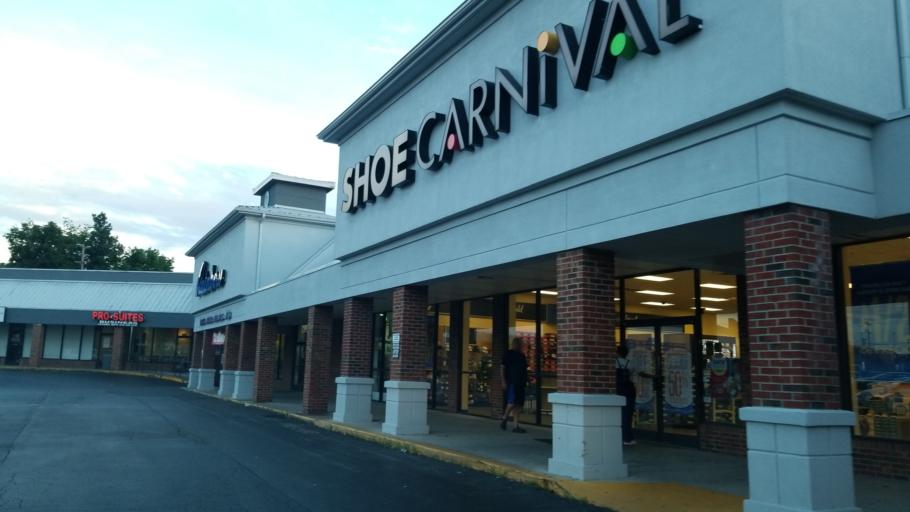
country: US
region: Tennessee
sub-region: Rutherford County
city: La Vergne
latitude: 36.0473
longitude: -86.6503
